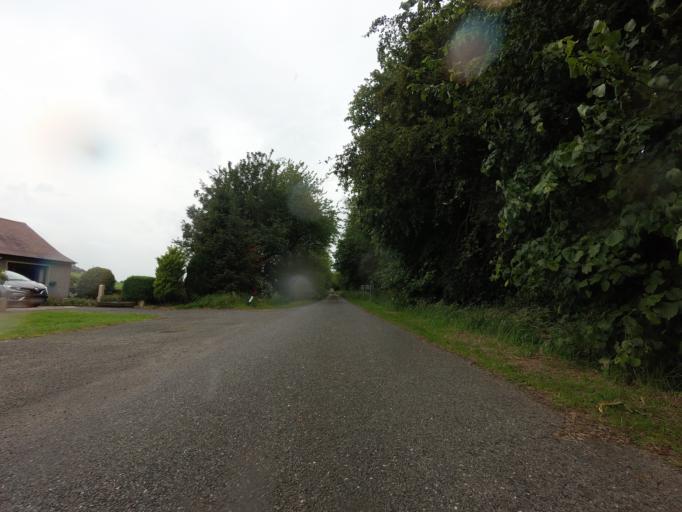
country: GB
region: Scotland
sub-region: Moray
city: Cullen
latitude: 57.6741
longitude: -2.7814
